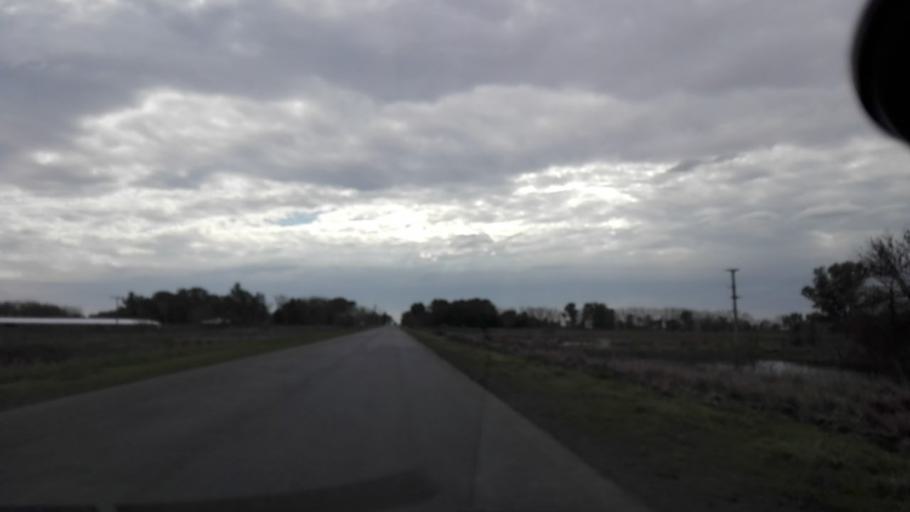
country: AR
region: Buenos Aires
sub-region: Partido de Las Flores
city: Las Flores
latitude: -36.2254
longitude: -59.0446
